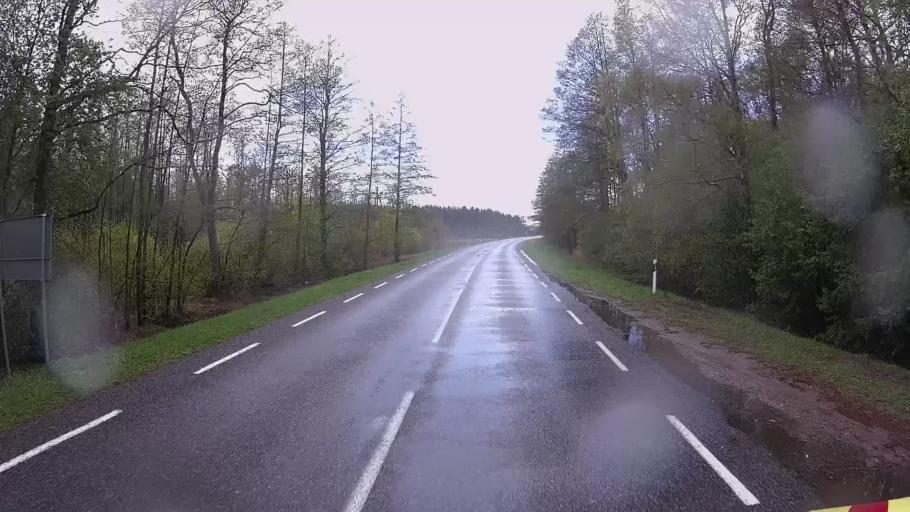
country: EE
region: Hiiumaa
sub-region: Kaerdla linn
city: Kardla
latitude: 58.8325
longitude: 22.8210
